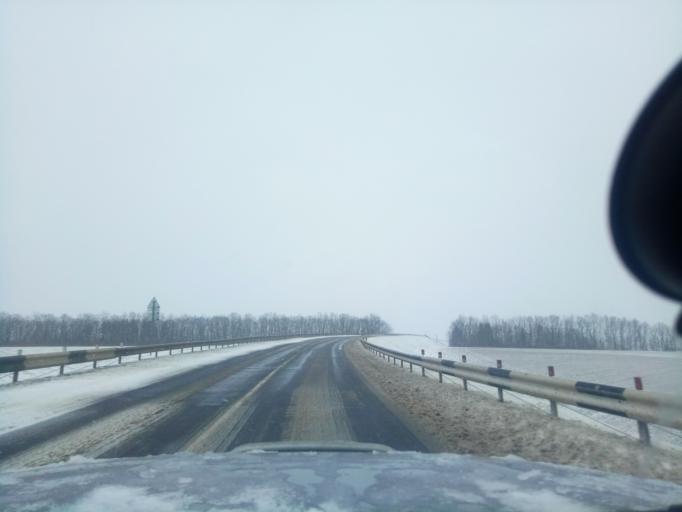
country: BY
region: Minsk
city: Haradzyeya
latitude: 53.3322
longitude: 26.5446
